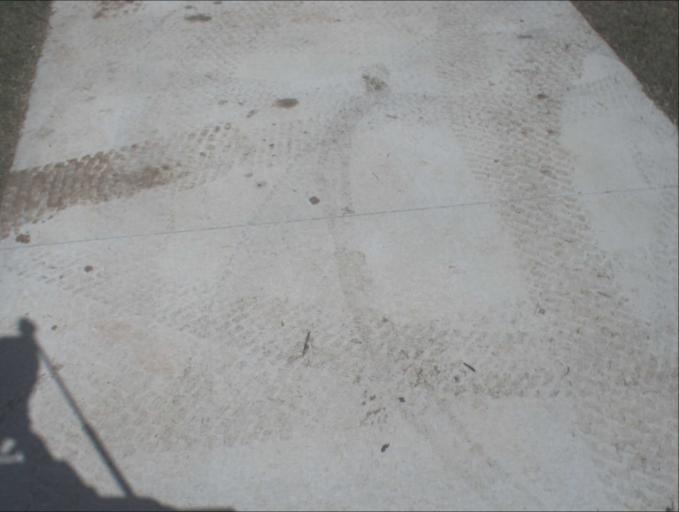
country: AU
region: Queensland
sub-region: Logan
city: Chambers Flat
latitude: -27.7773
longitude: 153.0967
